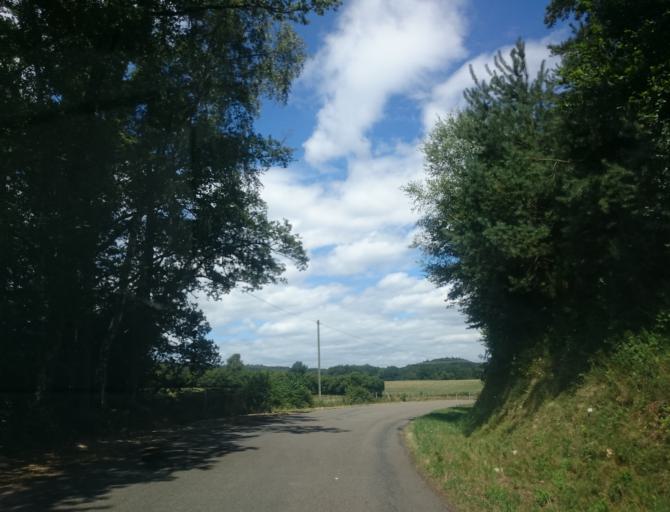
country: FR
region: Auvergne
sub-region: Departement du Cantal
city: Laroquebrou
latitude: 44.9102
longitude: 2.1885
